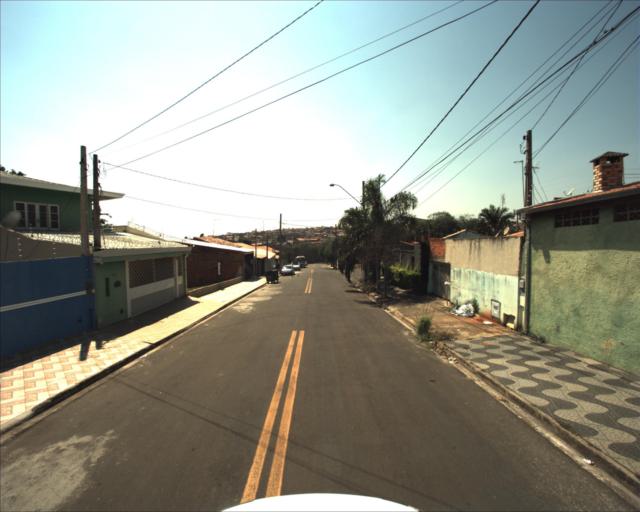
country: BR
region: Sao Paulo
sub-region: Sorocaba
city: Sorocaba
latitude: -23.4577
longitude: -47.4949
